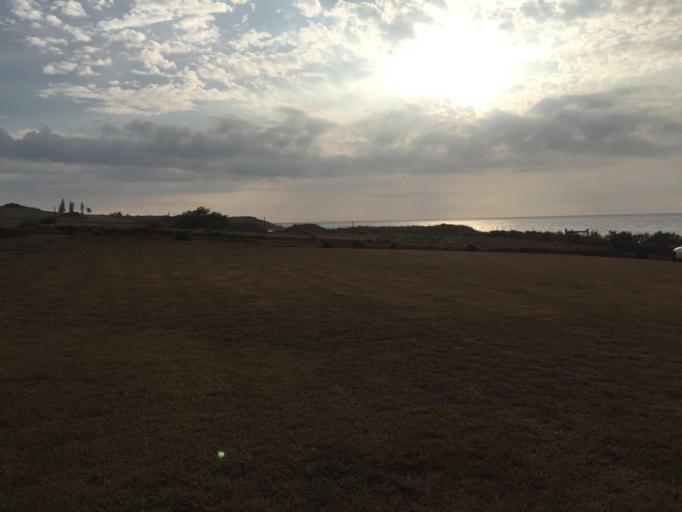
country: US
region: Hawaii
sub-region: Hawaii County
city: Hawi
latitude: 20.2559
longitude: -155.8832
